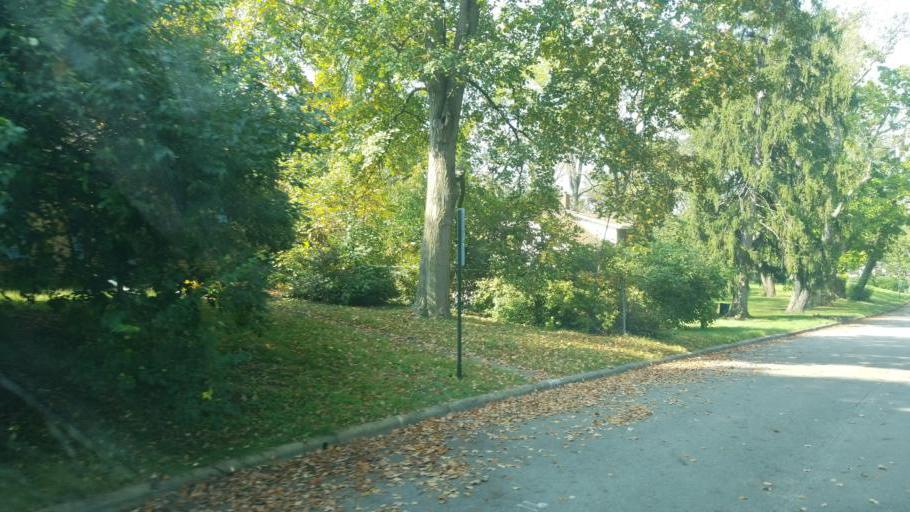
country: US
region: Ohio
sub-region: Franklin County
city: Worthington
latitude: 40.0725
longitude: -83.0299
